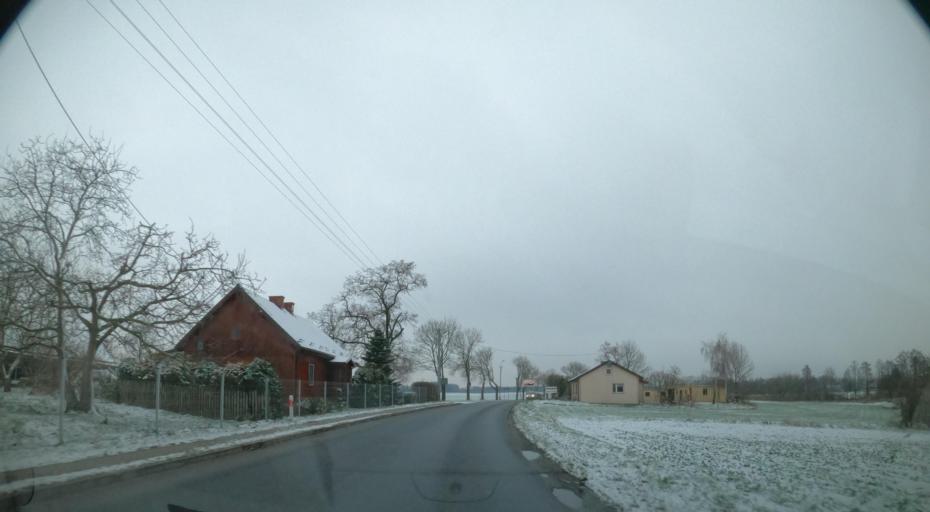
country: PL
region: Kujawsko-Pomorskie
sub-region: Powiat lipnowski
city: Wielgie
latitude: 52.6918
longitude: 19.2791
